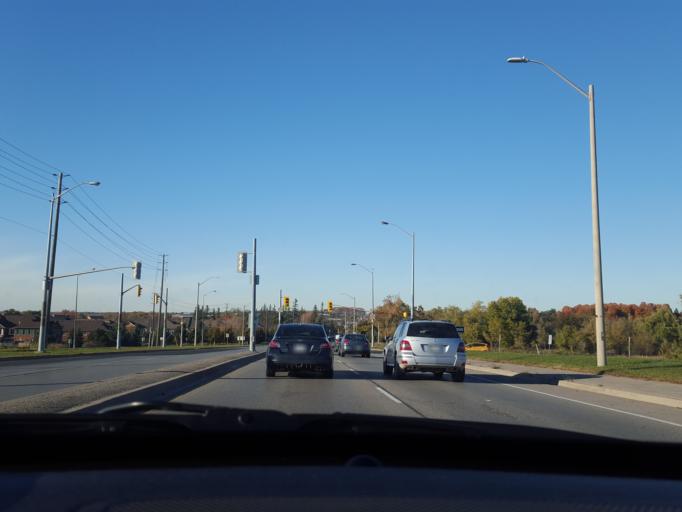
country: CA
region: Ontario
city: Markham
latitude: 43.8571
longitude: -79.2817
